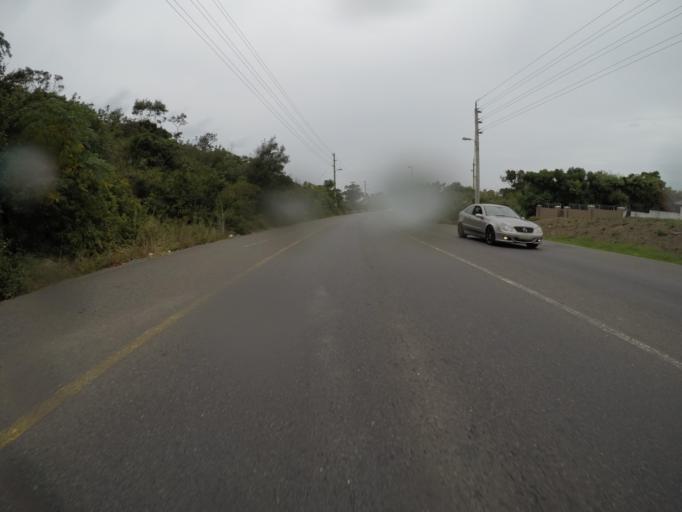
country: ZA
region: Eastern Cape
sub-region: Buffalo City Metropolitan Municipality
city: East London
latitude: -32.9988
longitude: 27.8401
